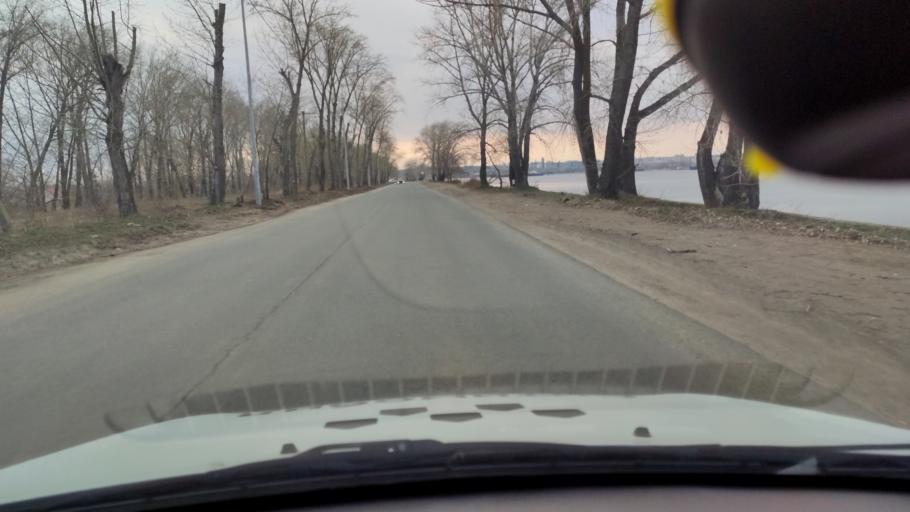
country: RU
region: Samara
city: Zhigulevsk
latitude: 53.4570
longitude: 49.5423
